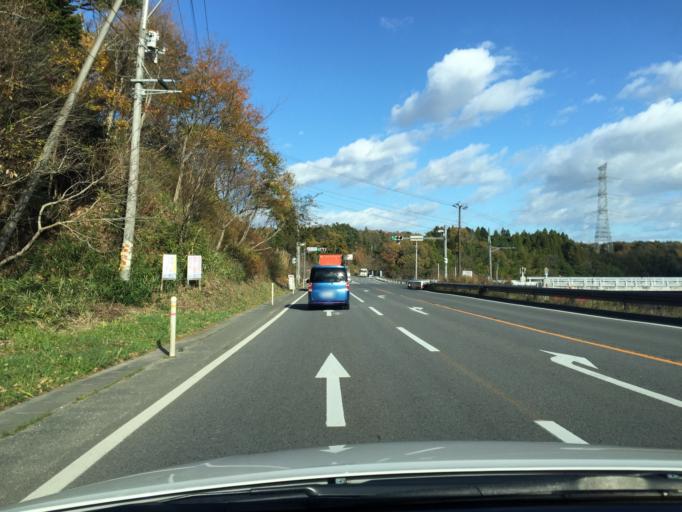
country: JP
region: Fukushima
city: Namie
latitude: 37.3122
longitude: 141.0007
